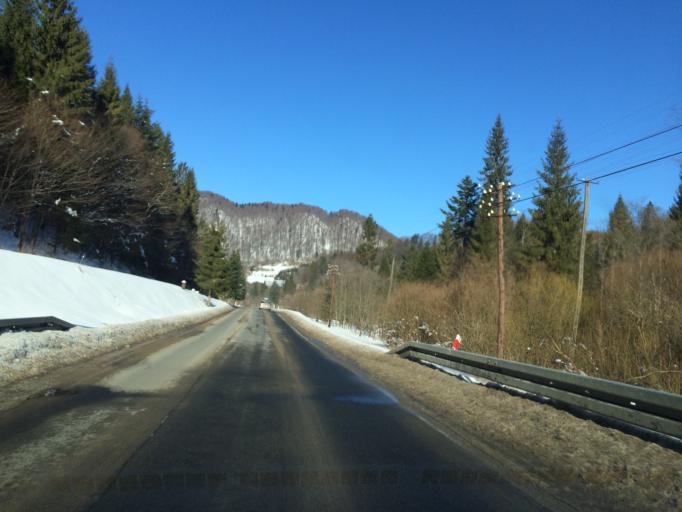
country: PL
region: Subcarpathian Voivodeship
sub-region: Powiat leski
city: Cisna
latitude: 49.2184
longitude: 22.3651
